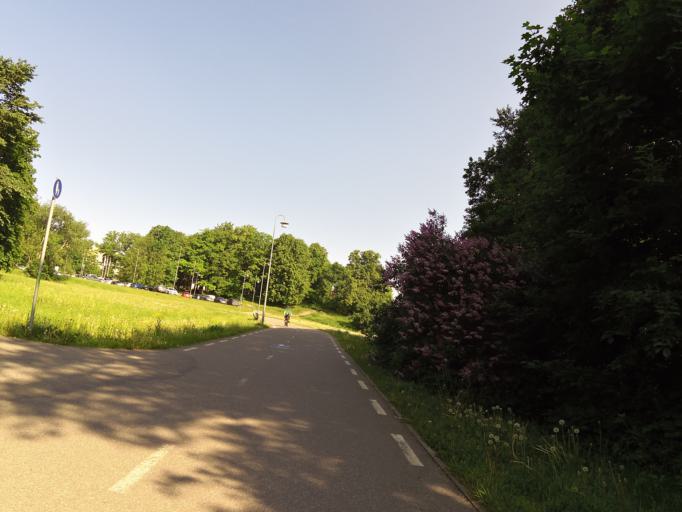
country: EE
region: Harju
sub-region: Saue vald
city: Laagri
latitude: 59.4297
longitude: 24.6531
